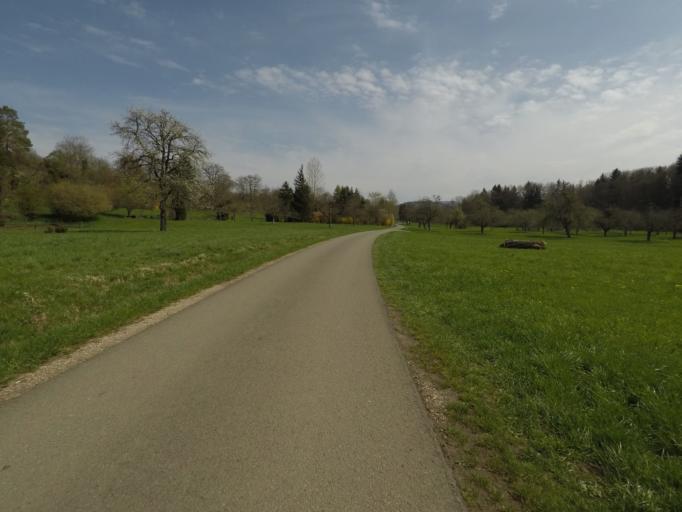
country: DE
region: Baden-Wuerttemberg
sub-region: Tuebingen Region
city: Reutlingen
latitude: 48.4849
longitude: 9.1738
